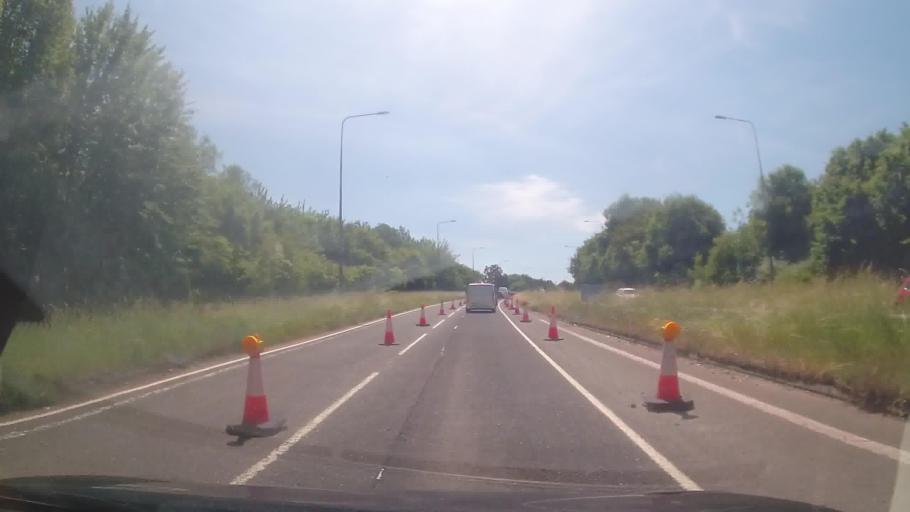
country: GB
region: England
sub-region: South Gloucestershire
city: Kingswood
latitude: 51.4585
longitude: -2.4821
